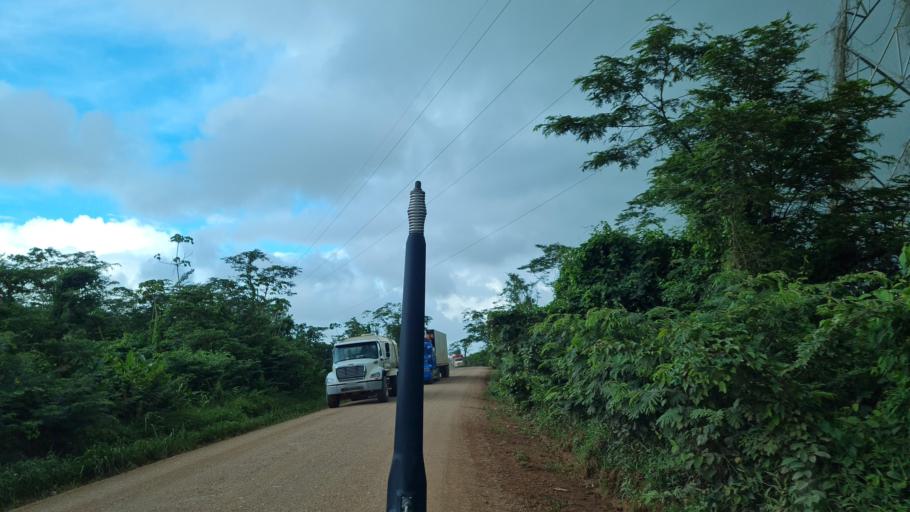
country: NI
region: Atlantico Norte (RAAN)
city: Puerto Cabezas
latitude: 14.1067
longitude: -83.6793
